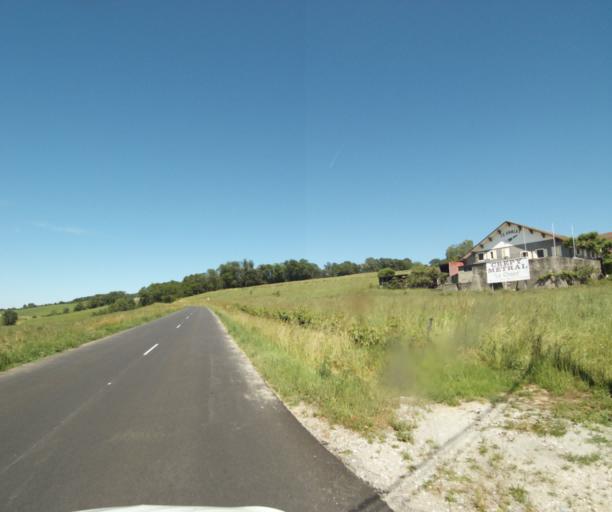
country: FR
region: Rhone-Alpes
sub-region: Departement de la Haute-Savoie
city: Loisin
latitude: 46.2904
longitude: 6.3151
